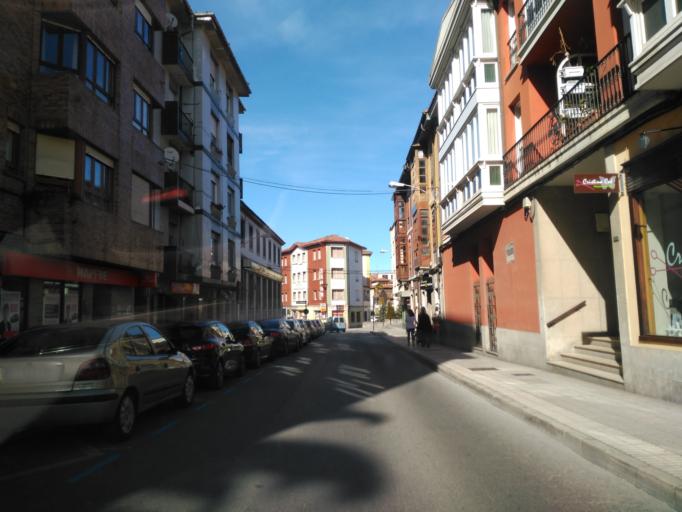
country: ES
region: Asturias
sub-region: Province of Asturias
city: Llanes
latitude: 43.4180
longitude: -4.7536
